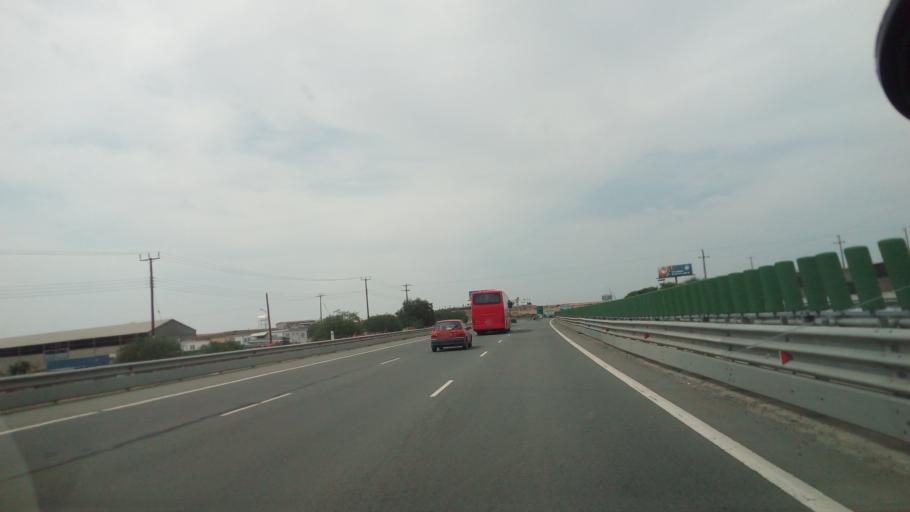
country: CY
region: Lefkosia
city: Alampra
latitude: 35.0190
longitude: 33.3813
